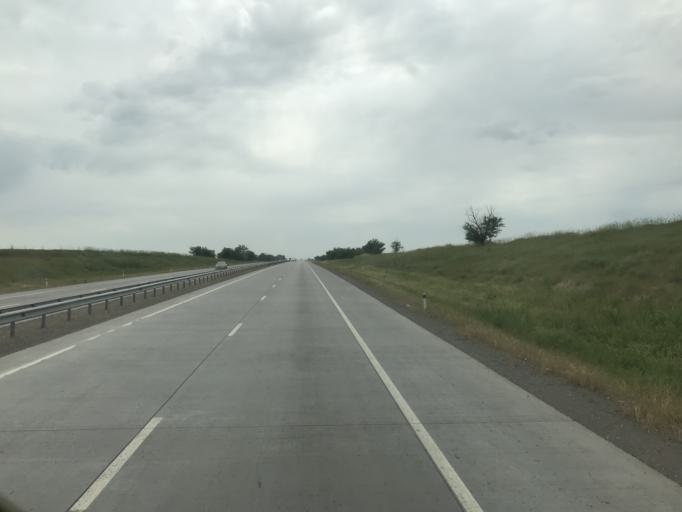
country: KZ
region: Ongtustik Qazaqstan
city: Shymkent
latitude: 42.1990
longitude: 69.5088
